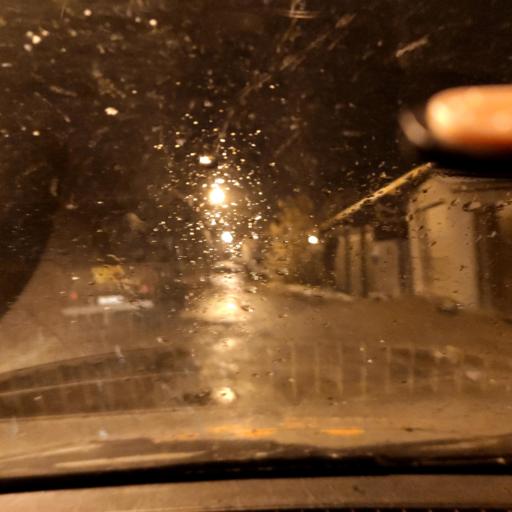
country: RU
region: Bashkortostan
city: Ufa
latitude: 54.7340
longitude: 55.9004
